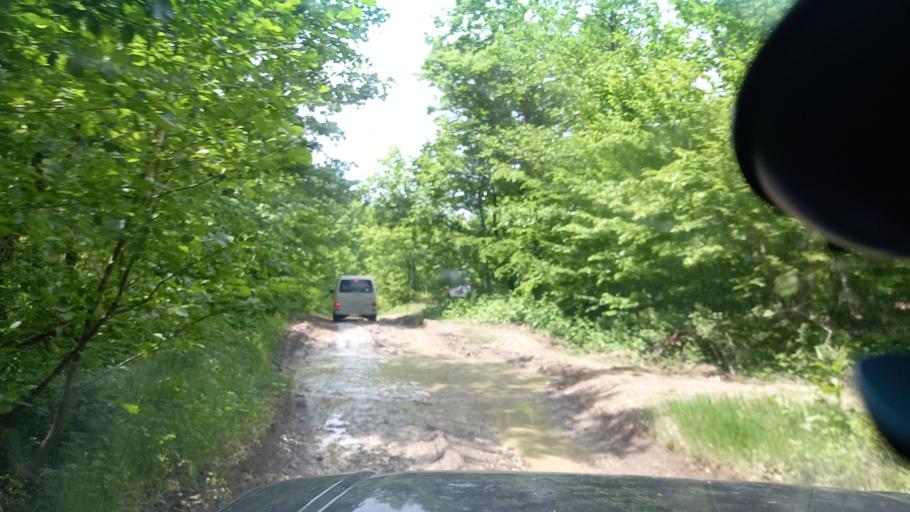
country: RU
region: Krasnodarskiy
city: Tuapse
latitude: 44.2646
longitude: 39.2728
